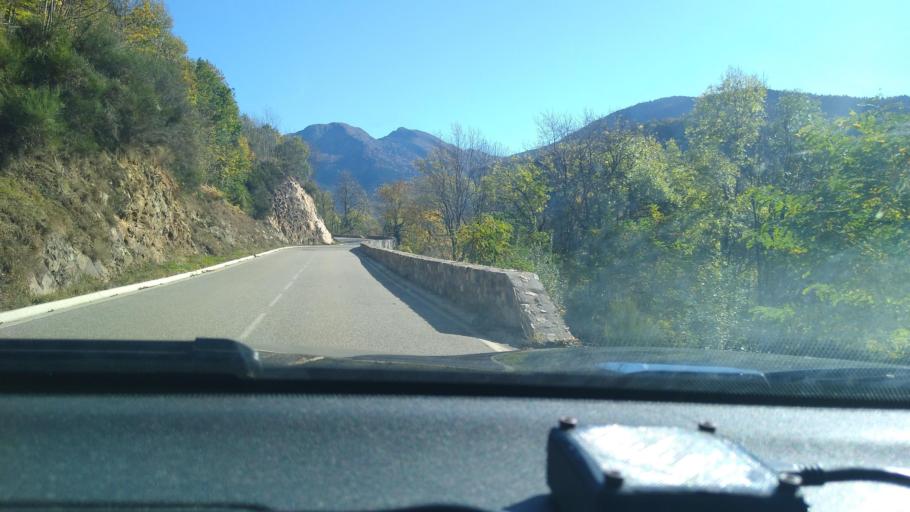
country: FR
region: Midi-Pyrenees
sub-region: Departement de l'Ariege
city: Ax-les-Thermes
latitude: 42.7222
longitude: 1.8586
